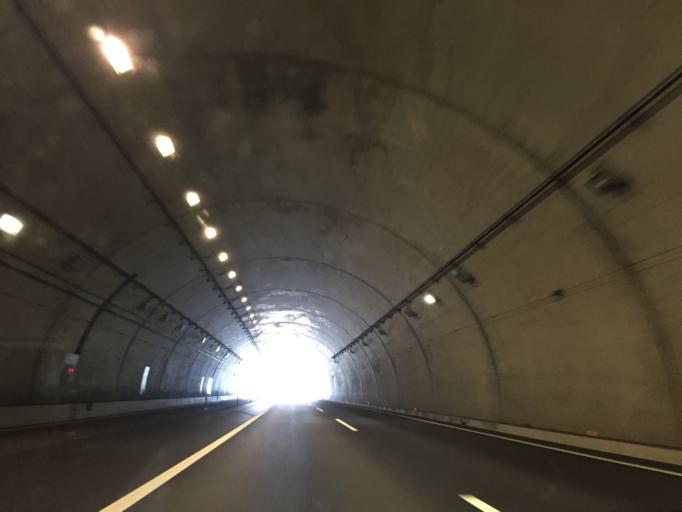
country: JP
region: Shizuoka
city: Fujinomiya
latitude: 35.1849
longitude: 138.6159
